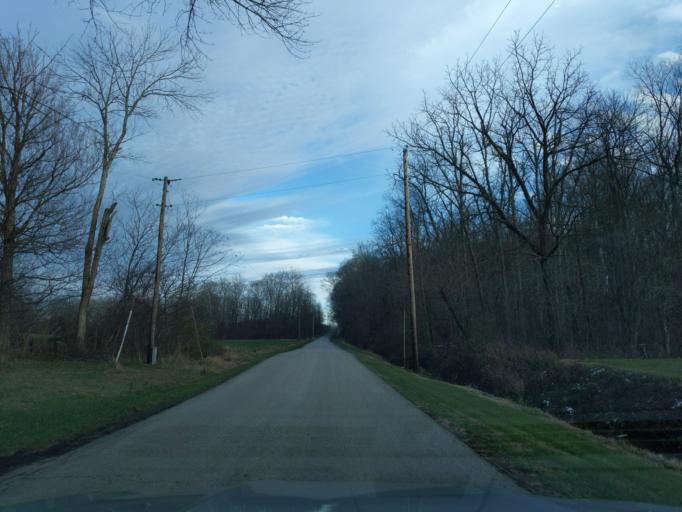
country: US
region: Indiana
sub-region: Decatur County
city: Westport
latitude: 39.2195
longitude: -85.5037
